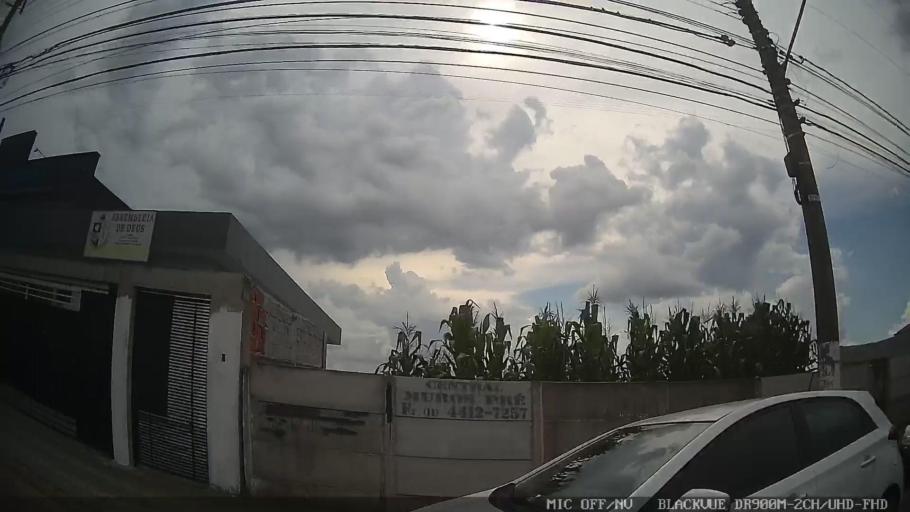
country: BR
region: Sao Paulo
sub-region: Atibaia
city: Atibaia
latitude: -23.1446
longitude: -46.5534
